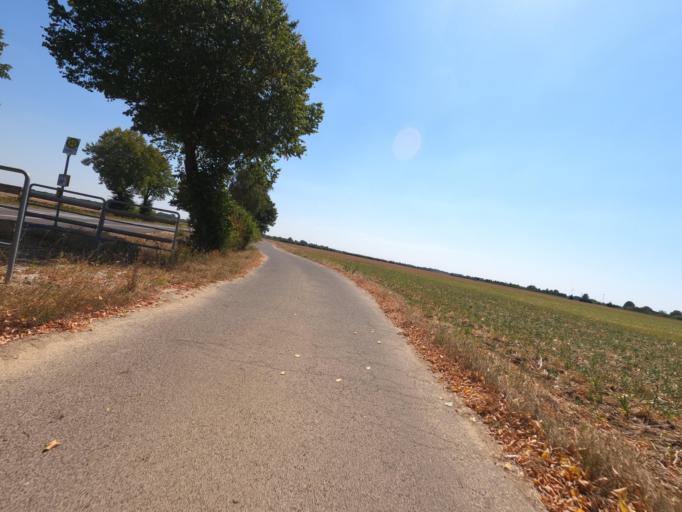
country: DE
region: North Rhine-Westphalia
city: Erkelenz
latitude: 51.1070
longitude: 6.2950
